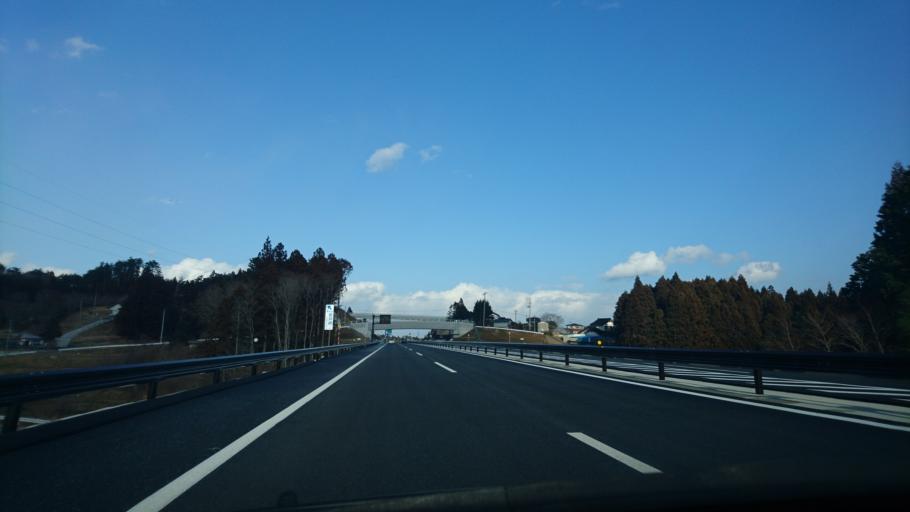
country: JP
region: Iwate
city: Ofunato
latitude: 38.8105
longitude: 141.5484
